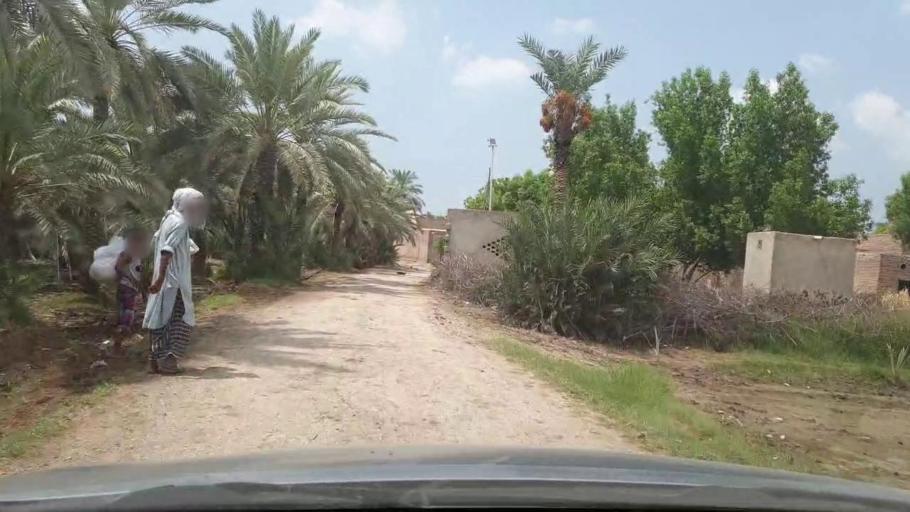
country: PK
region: Sindh
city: Kot Diji
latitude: 27.4046
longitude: 68.7564
